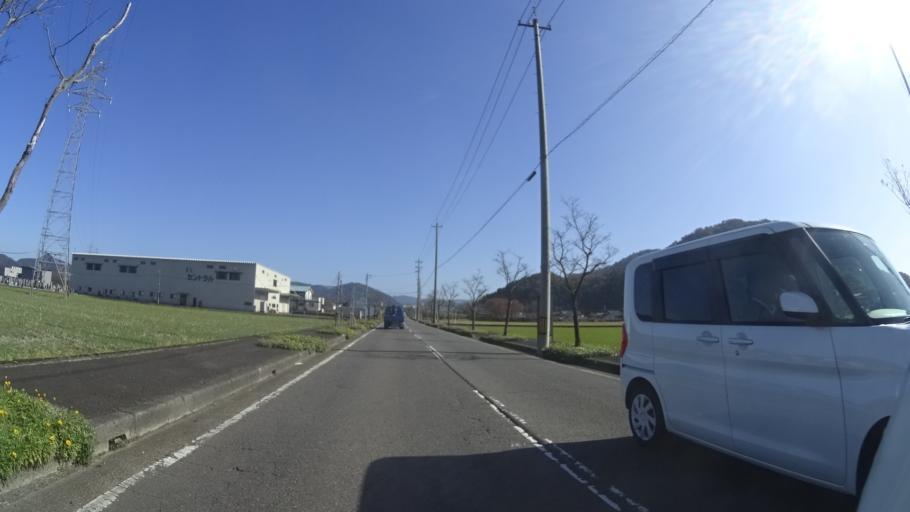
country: JP
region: Fukui
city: Sabae
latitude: 35.9496
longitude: 136.2046
